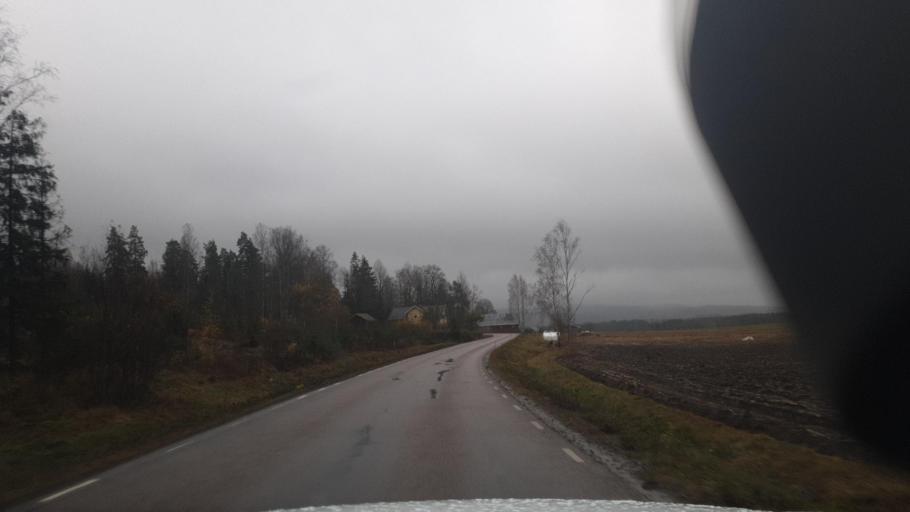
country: SE
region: Vaermland
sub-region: Eda Kommun
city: Charlottenberg
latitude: 59.7513
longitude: 12.1594
